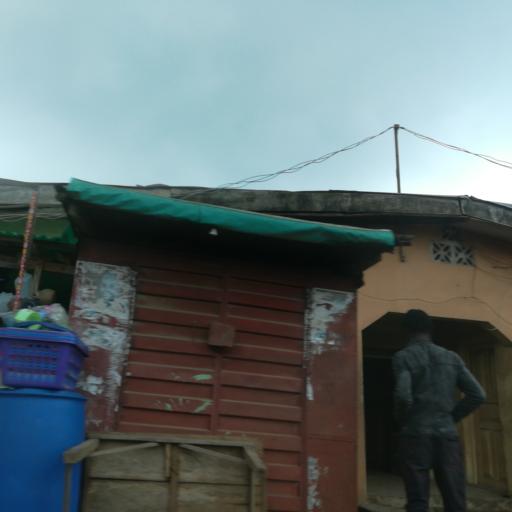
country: NG
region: Lagos
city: Agege
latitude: 6.5988
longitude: 3.3003
